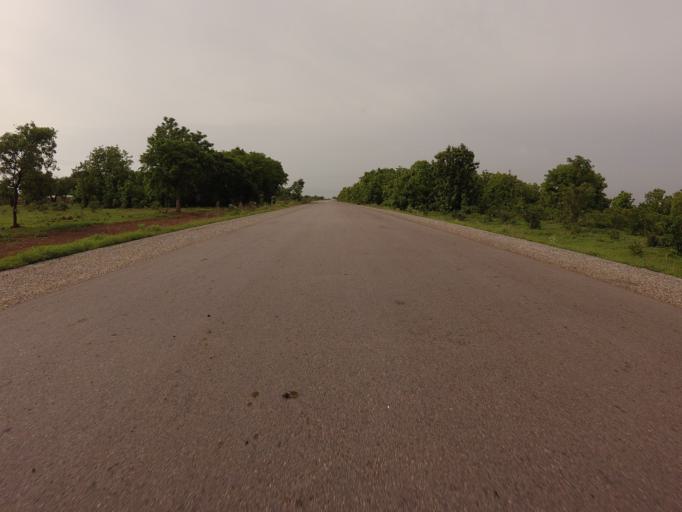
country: GH
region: Northern
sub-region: Yendi
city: Yendi
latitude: 9.6252
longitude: -0.0547
